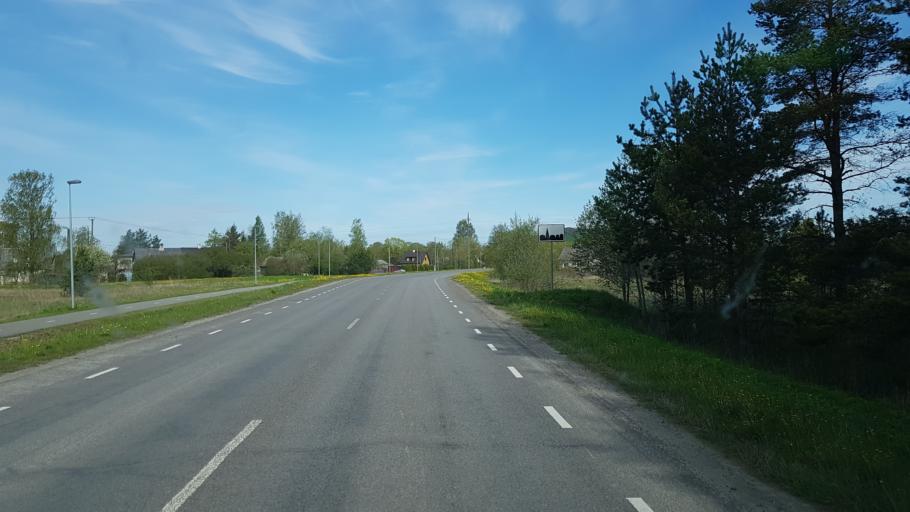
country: EE
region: Ida-Virumaa
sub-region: Kivioli linn
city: Kivioli
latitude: 59.3485
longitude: 26.9698
